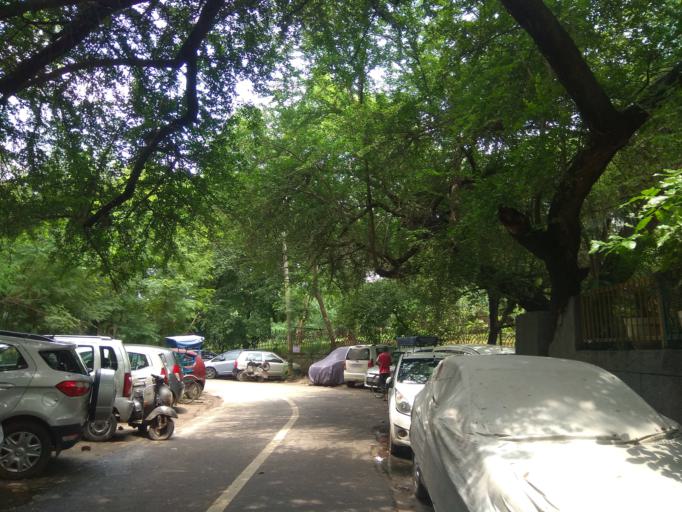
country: IN
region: NCT
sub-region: New Delhi
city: New Delhi
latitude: 28.5680
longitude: 77.2498
